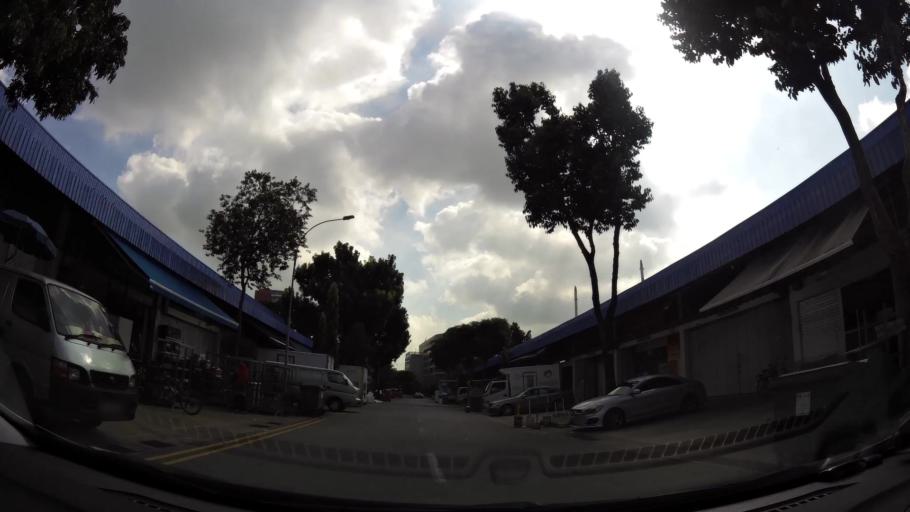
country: SG
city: Singapore
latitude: 1.3212
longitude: 103.8896
